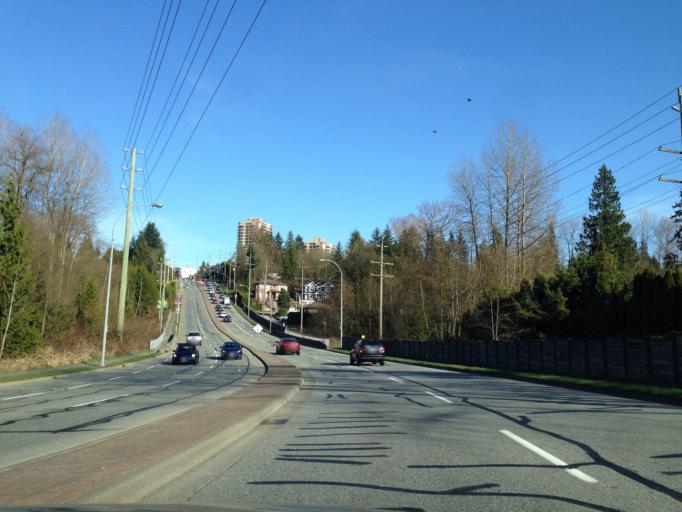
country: CA
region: British Columbia
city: Port Moody
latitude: 49.2632
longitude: -122.8989
